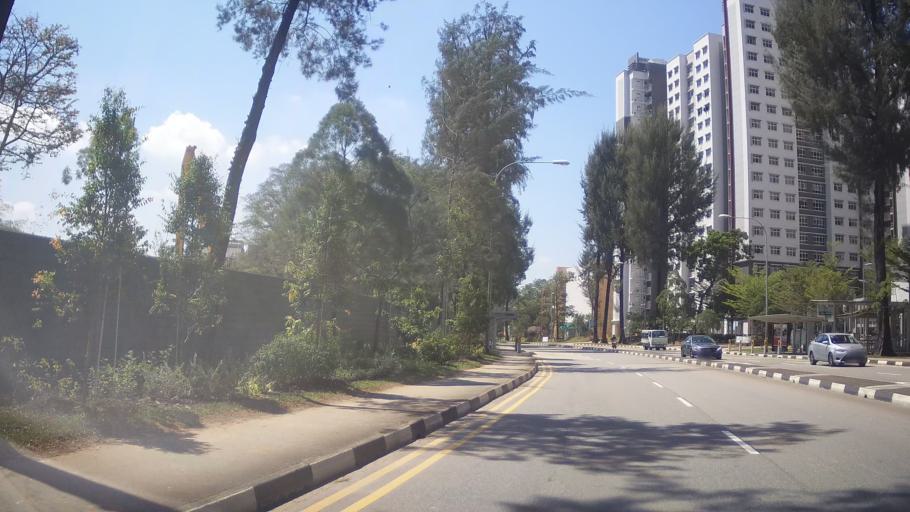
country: SG
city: Singapore
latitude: 1.3290
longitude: 103.7249
